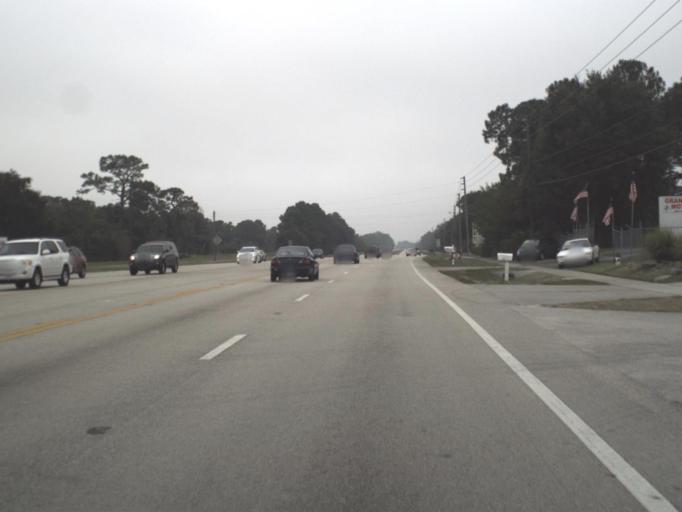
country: US
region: Florida
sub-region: Brevard County
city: June Park
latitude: 28.0303
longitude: -80.6717
